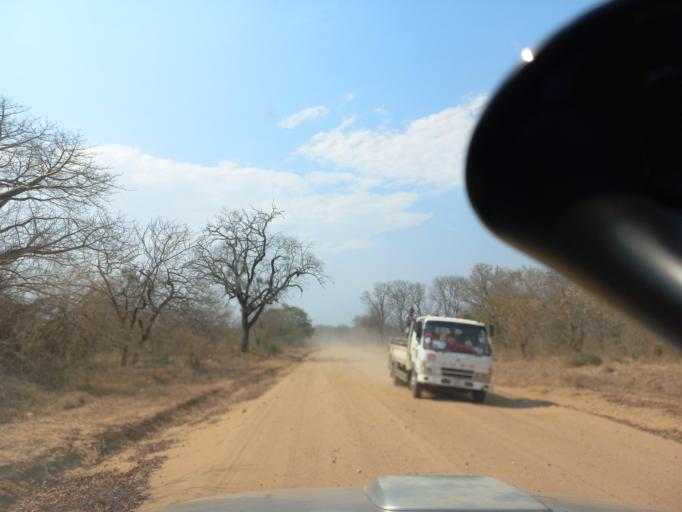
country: ZW
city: Chirundu
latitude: -15.9334
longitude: 28.9152
